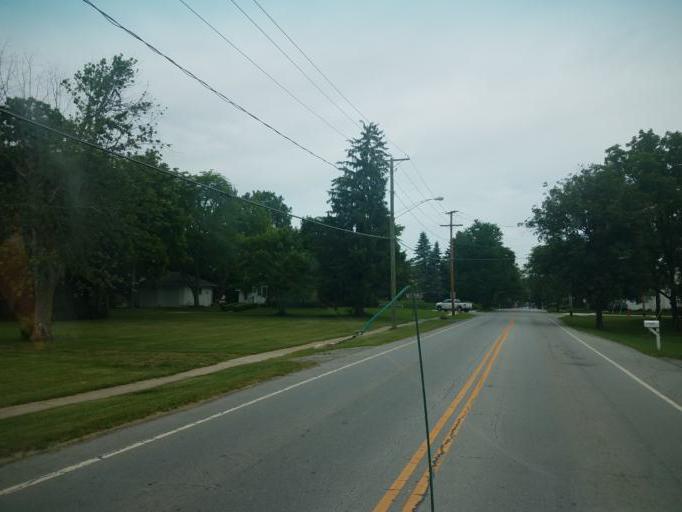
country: US
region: Ohio
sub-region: Hardin County
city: Ada
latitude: 40.7613
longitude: -83.8232
